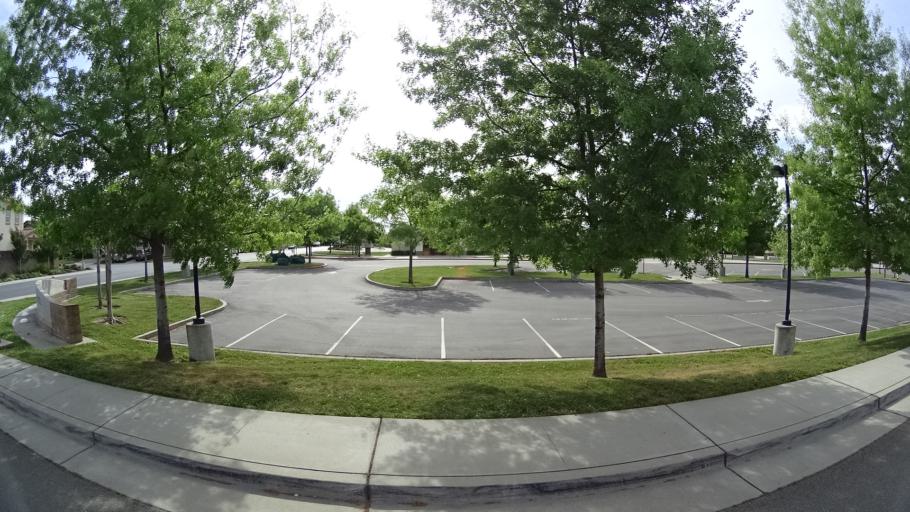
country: US
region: California
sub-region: Placer County
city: Rocklin
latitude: 38.8291
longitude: -121.2753
